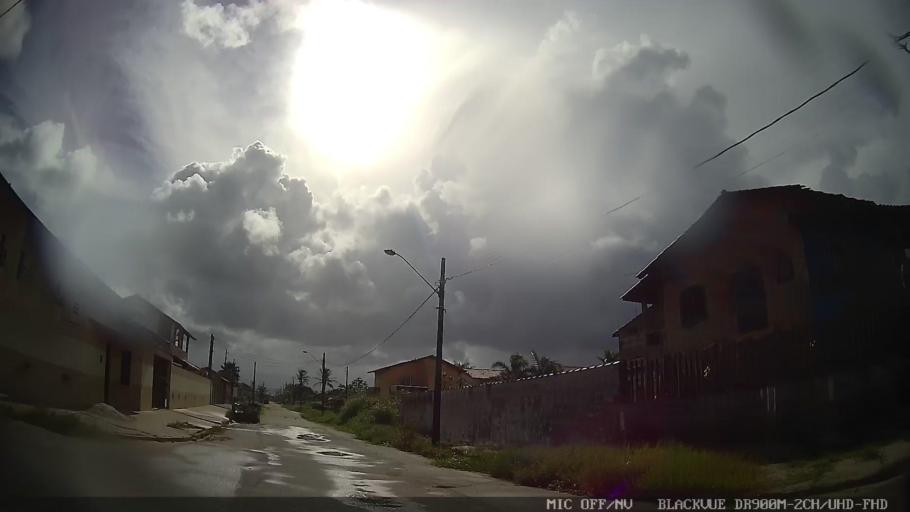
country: BR
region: Sao Paulo
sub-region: Itanhaem
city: Itanhaem
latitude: -24.2390
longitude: -46.8762
